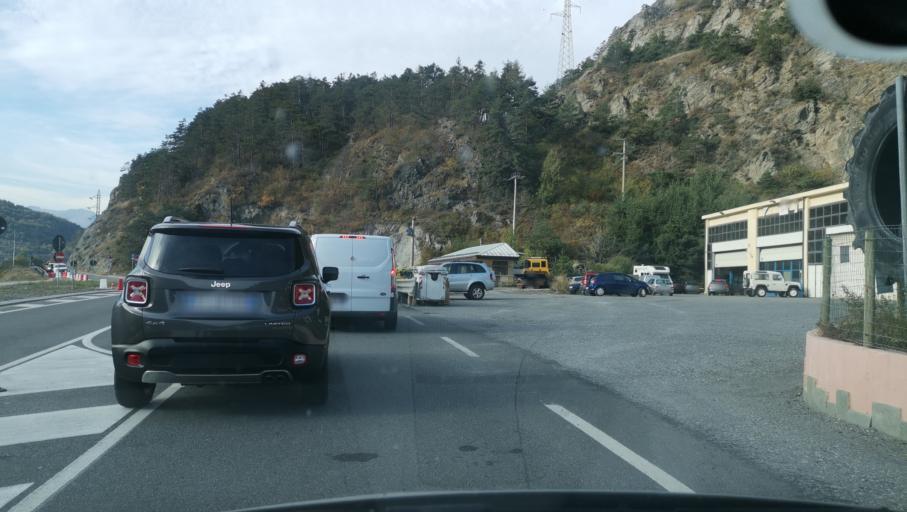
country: IT
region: Piedmont
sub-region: Provincia di Torino
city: Sauze d'Oulx
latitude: 45.0533
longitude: 6.8555
